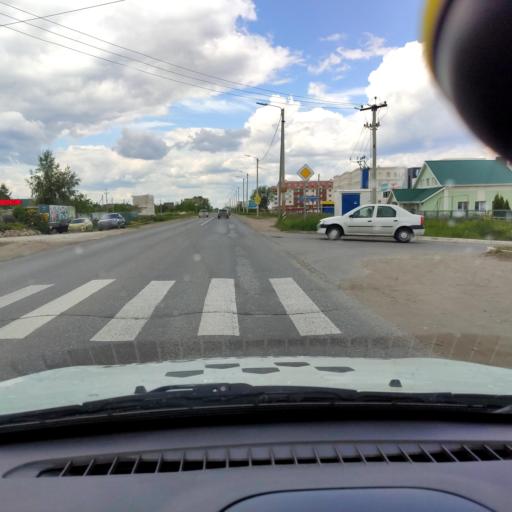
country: RU
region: Samara
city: Podstepki
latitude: 53.5210
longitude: 49.1932
